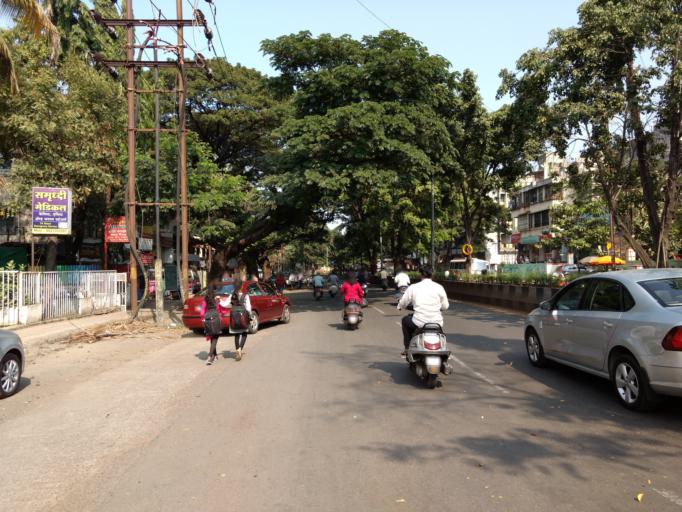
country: IN
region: Maharashtra
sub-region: Pune Division
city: Pune
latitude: 18.4760
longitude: 73.8623
